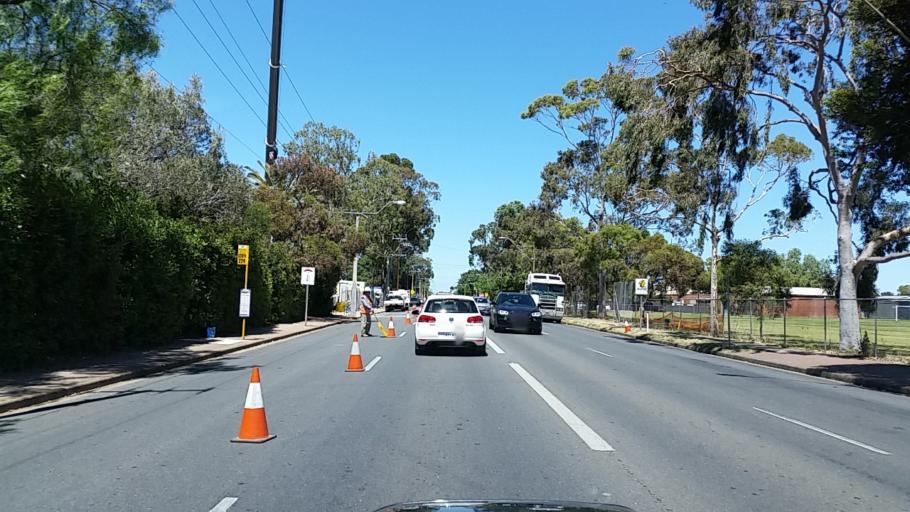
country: AU
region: South Australia
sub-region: Charles Sturt
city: Woodville North
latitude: -34.8731
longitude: 138.5426
